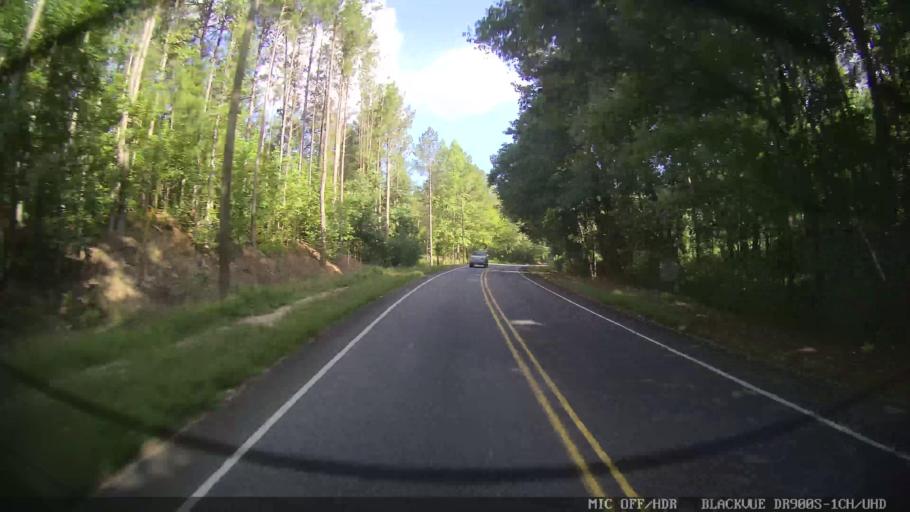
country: US
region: Georgia
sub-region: Floyd County
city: Lindale
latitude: 34.1893
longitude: -85.0576
